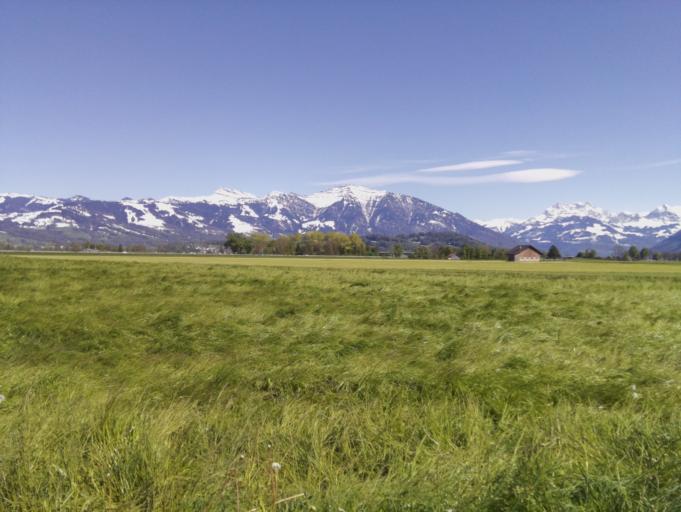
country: CH
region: Schwyz
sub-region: Bezirk March
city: Tuggen
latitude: 47.2068
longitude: 8.9597
